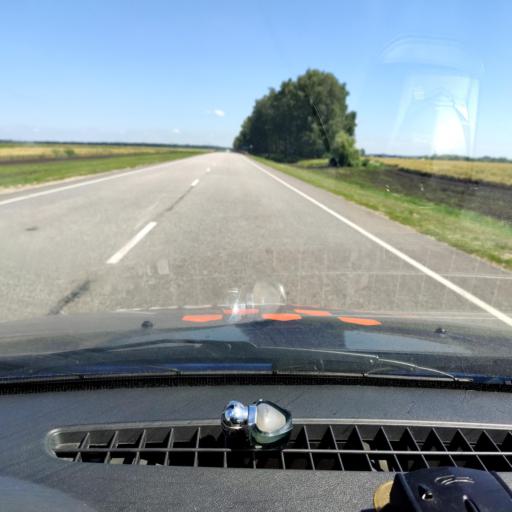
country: RU
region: Orjol
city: Pokrovskoye
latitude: 52.6342
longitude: 36.6918
